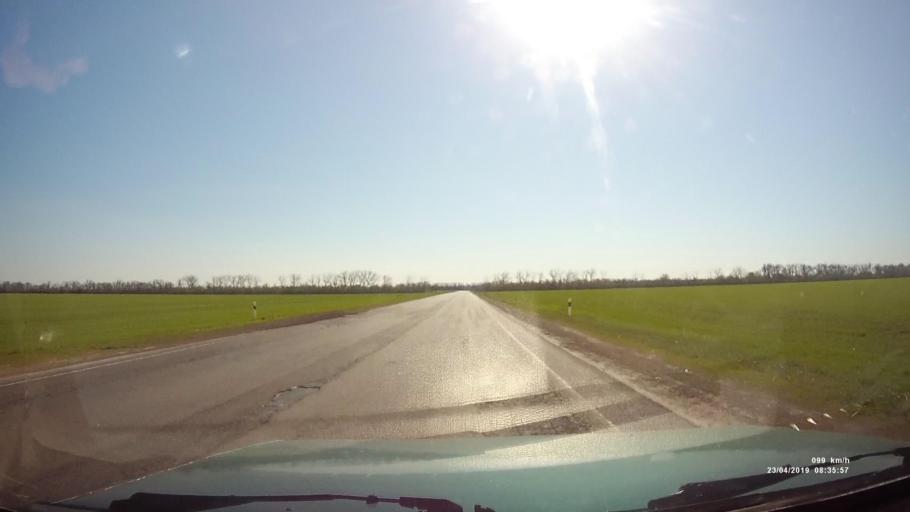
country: RU
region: Rostov
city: Tselina
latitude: 46.5216
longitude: 41.1448
